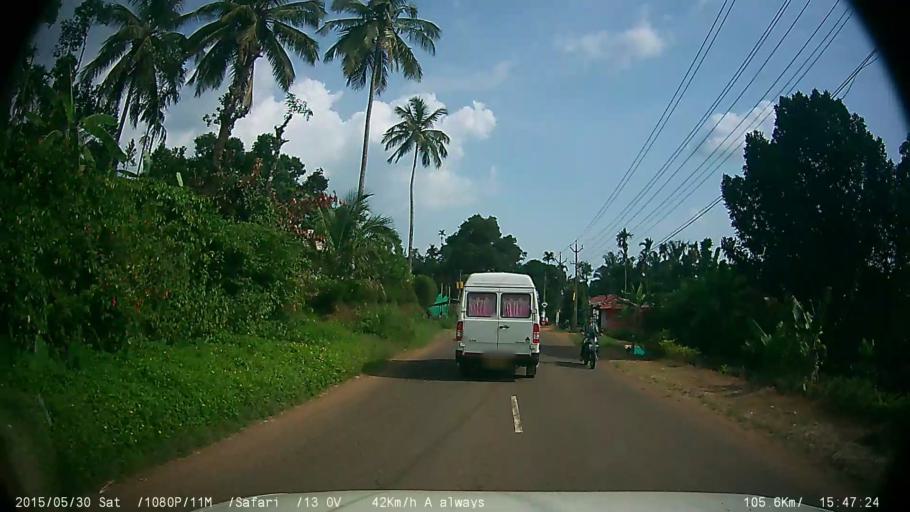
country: IN
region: Kerala
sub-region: Wayanad
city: Panamaram
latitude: 11.7046
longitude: 76.0784
